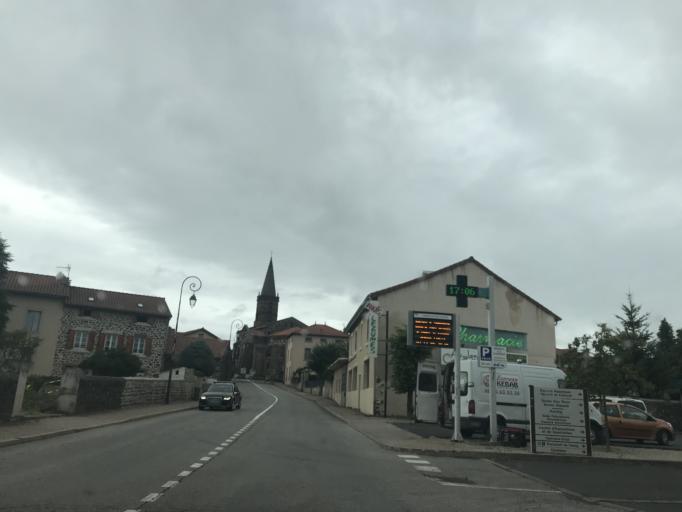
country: FR
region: Auvergne
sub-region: Departement de la Haute-Loire
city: Saint-Paulien
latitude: 45.1332
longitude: 3.8149
